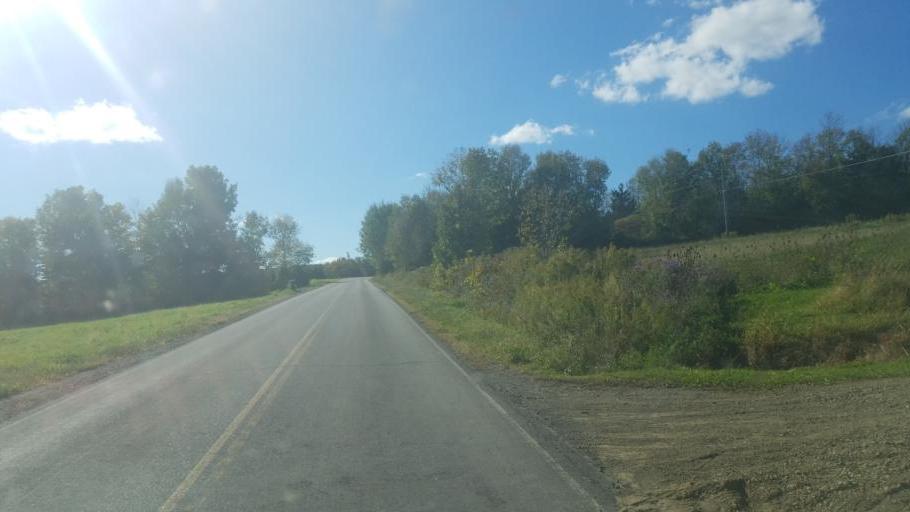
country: US
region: New York
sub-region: Allegany County
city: Friendship
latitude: 42.2758
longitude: -78.1427
